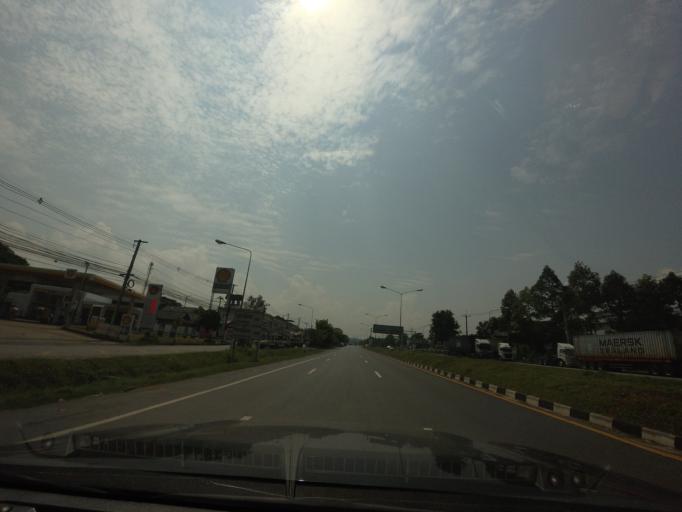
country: TH
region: Phrae
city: Den Chai
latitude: 17.9669
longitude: 100.0661
